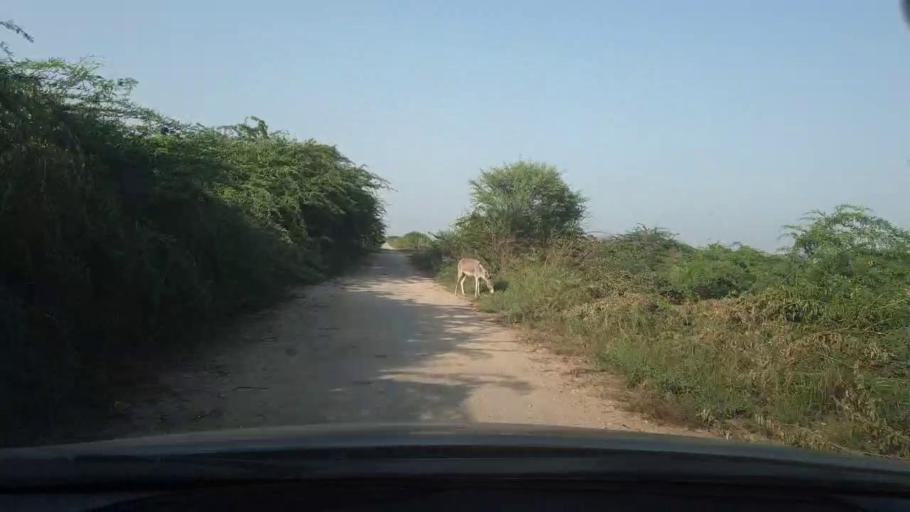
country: PK
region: Sindh
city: Naukot
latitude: 24.7719
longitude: 69.2311
